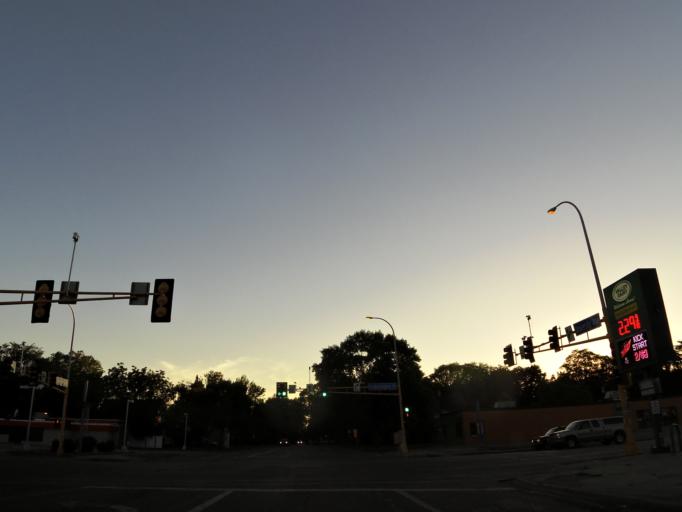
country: US
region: North Dakota
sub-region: Grand Forks County
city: Grand Forks
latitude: 47.9223
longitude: -97.0445
